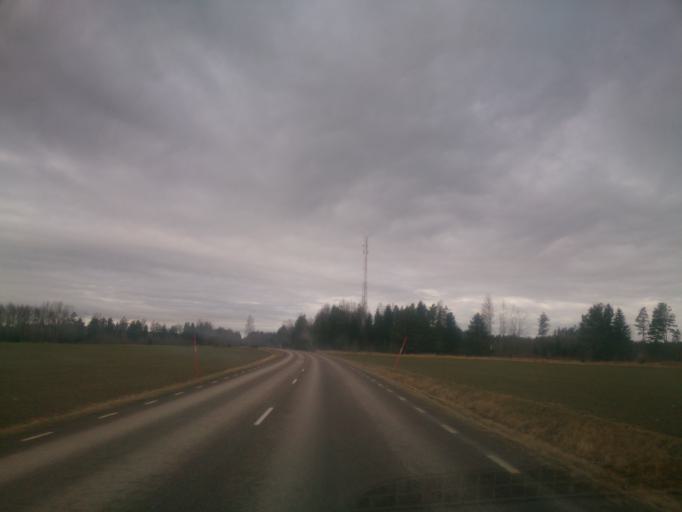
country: SE
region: OEstergoetland
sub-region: Motala Kommun
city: Borensberg
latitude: 58.4954
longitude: 15.3256
